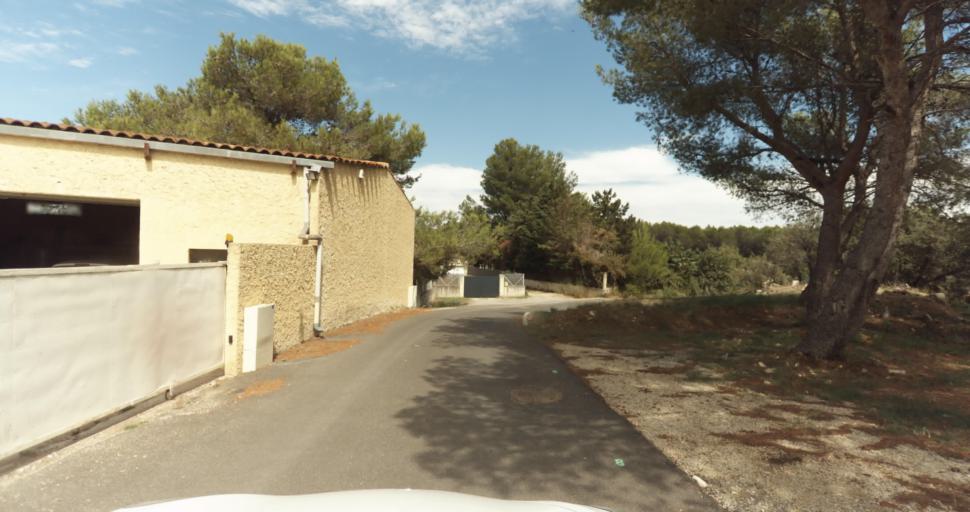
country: FR
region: Provence-Alpes-Cote d'Azur
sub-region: Departement des Bouches-du-Rhone
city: Miramas
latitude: 43.5812
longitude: 5.0243
